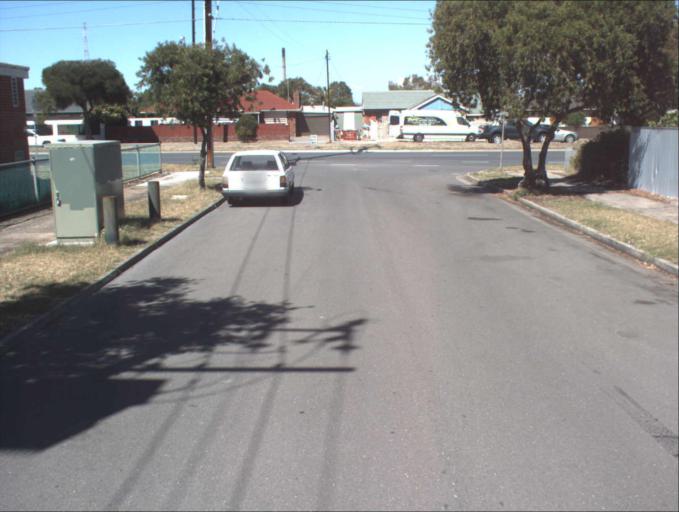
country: AU
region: South Australia
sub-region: Port Adelaide Enfield
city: Birkenhead
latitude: -34.8076
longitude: 138.5008
